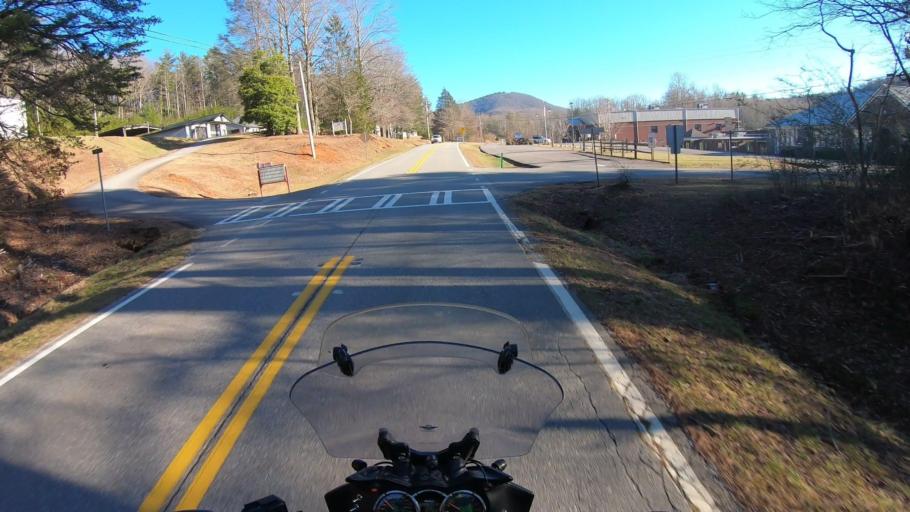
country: US
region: Georgia
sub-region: Lumpkin County
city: Dahlonega
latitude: 34.7050
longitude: -84.0375
